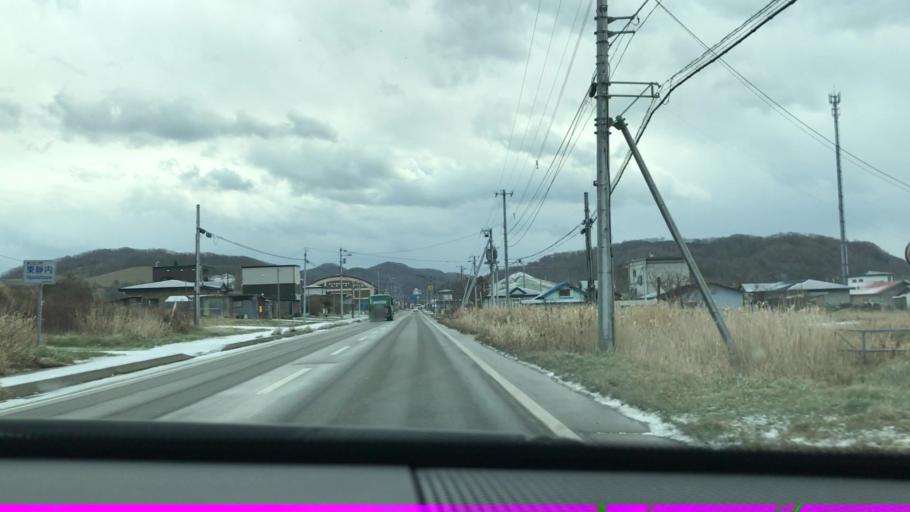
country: JP
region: Hokkaido
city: Shizunai-furukawacho
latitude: 42.3050
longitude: 142.4469
